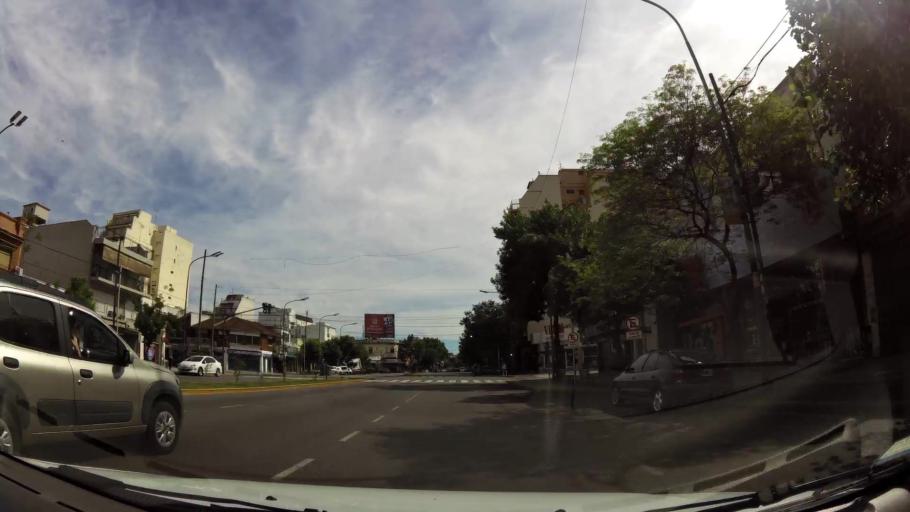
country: AR
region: Buenos Aires F.D.
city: Villa Lugano
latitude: -34.6528
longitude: -58.5039
